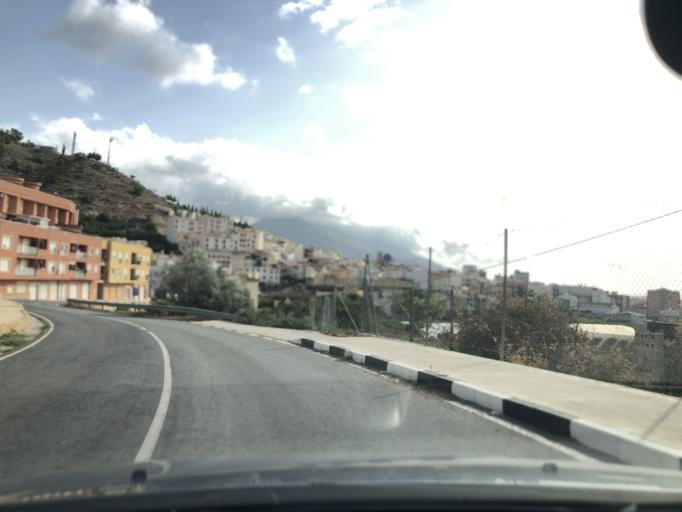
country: ES
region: Valencia
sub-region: Provincia de Alicante
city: Callosa d'En Sarria
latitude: 38.6510
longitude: -0.1301
